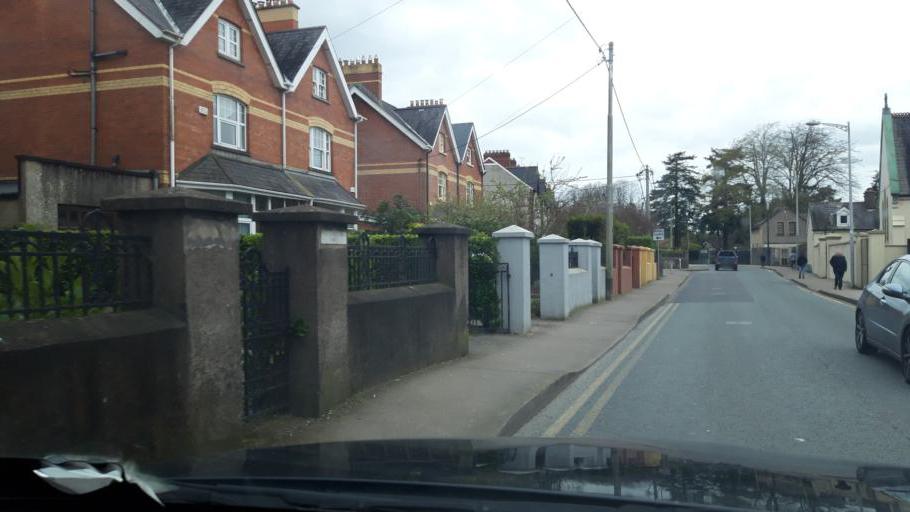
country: IE
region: Munster
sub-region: County Cork
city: Cork
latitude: 51.8910
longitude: -8.4978
